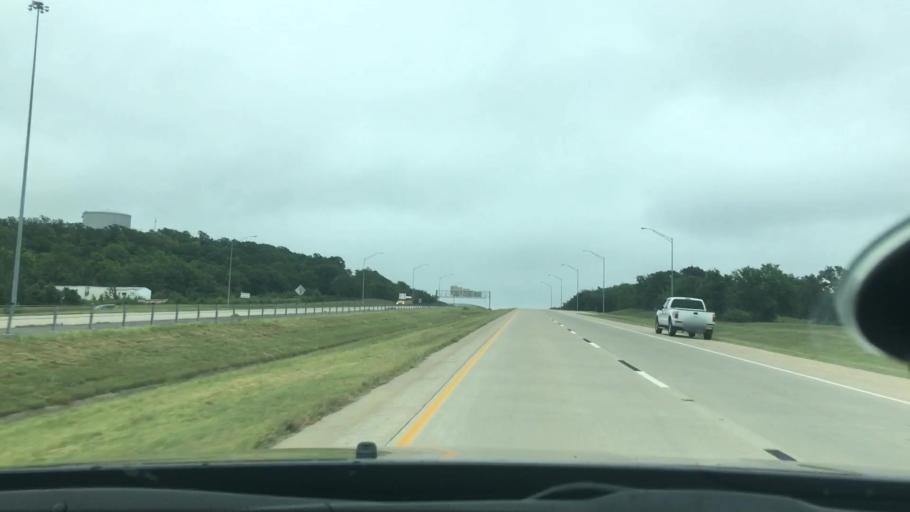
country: US
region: Oklahoma
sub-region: Okmulgee County
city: Henryetta
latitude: 35.4318
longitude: -95.9694
